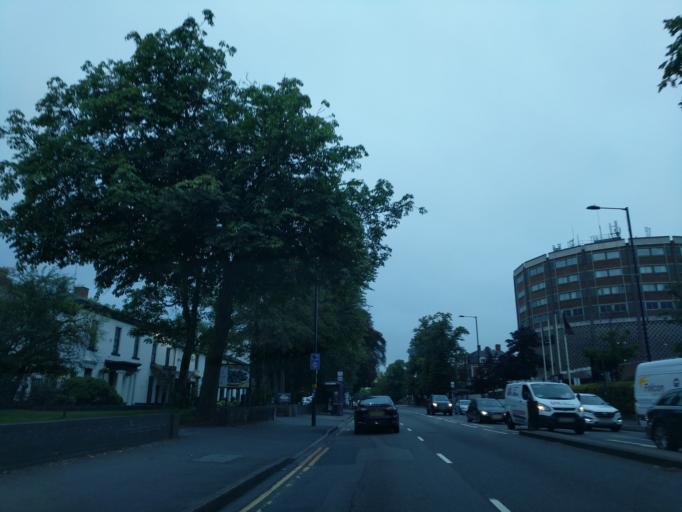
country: GB
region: England
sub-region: City and Borough of Birmingham
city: Hockley
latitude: 52.4719
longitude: -1.9367
